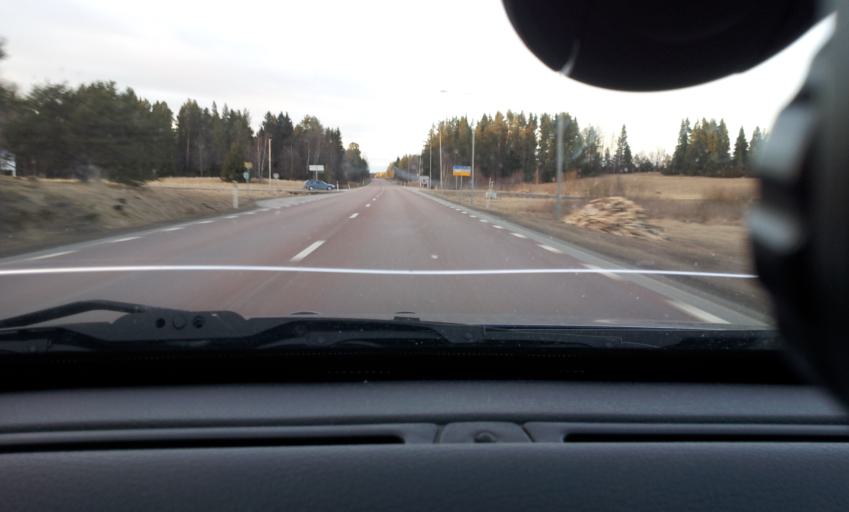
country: SE
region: Jaemtland
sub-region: Bergs Kommun
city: Hoverberg
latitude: 62.9245
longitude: 14.5346
